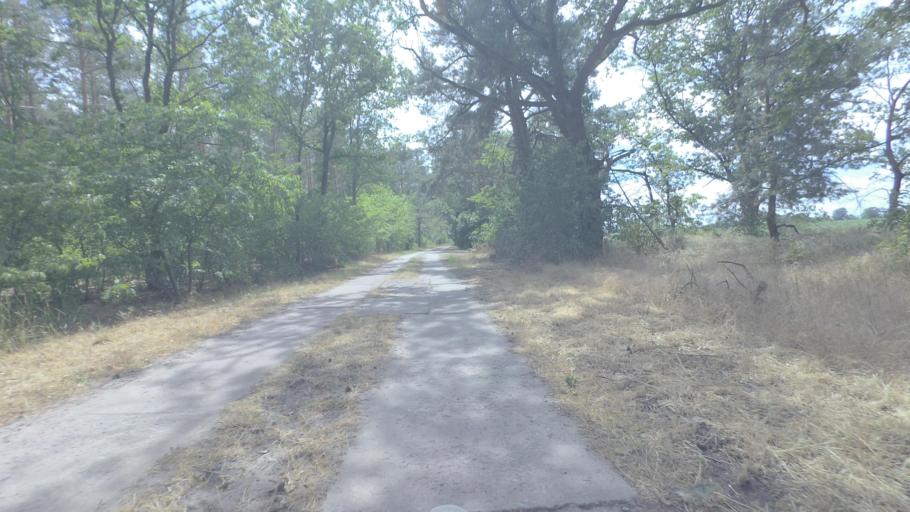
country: DE
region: Brandenburg
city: Stahnsdorf
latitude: 52.3505
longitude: 13.2303
